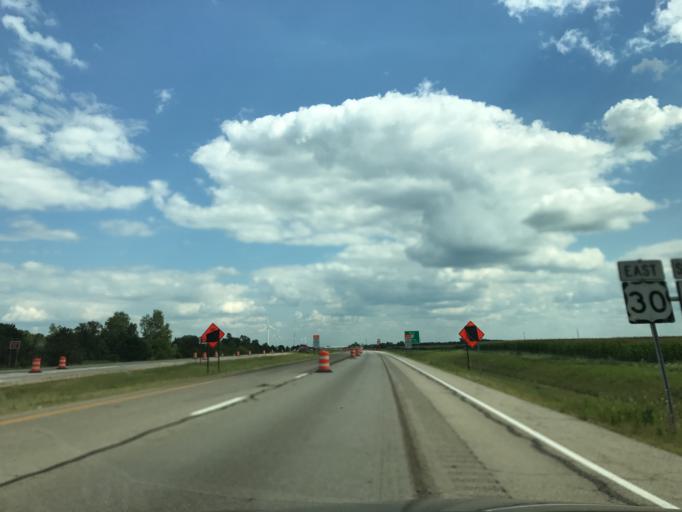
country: US
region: Ohio
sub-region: Van Wert County
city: Convoy
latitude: 40.9457
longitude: -84.7155
